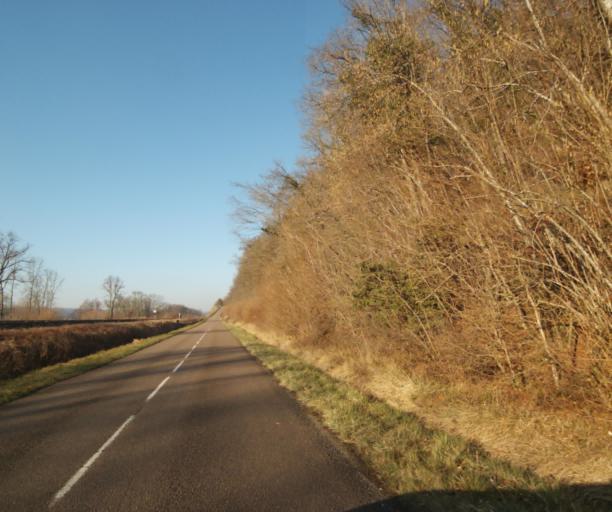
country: FR
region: Champagne-Ardenne
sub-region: Departement de la Haute-Marne
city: Chevillon
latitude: 48.5113
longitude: 5.1213
